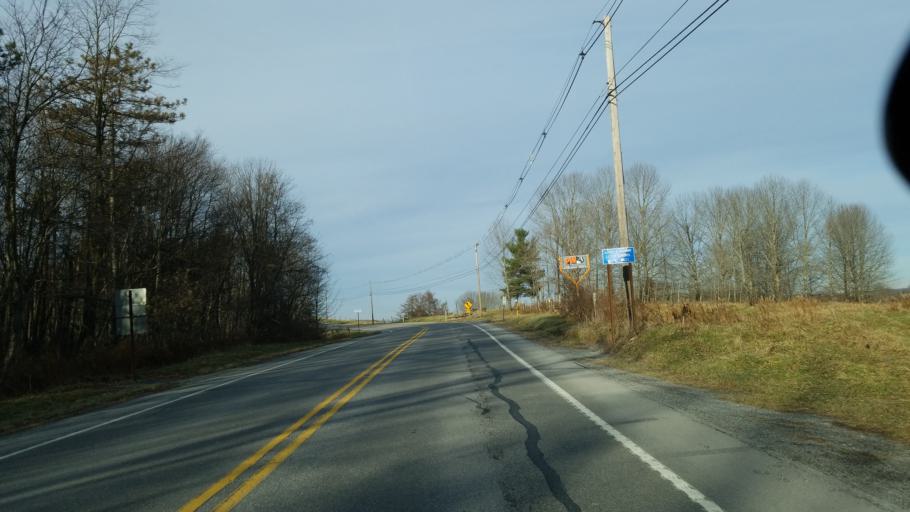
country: US
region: Pennsylvania
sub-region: Clearfield County
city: Curwensville
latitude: 40.9869
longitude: -78.6260
